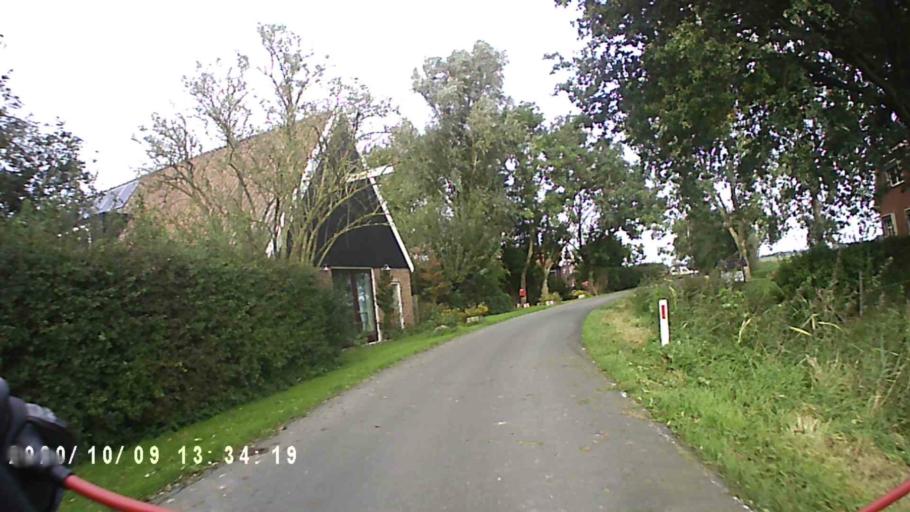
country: NL
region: Groningen
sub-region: Gemeente Zuidhorn
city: Aduard
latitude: 53.2918
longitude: 6.4693
